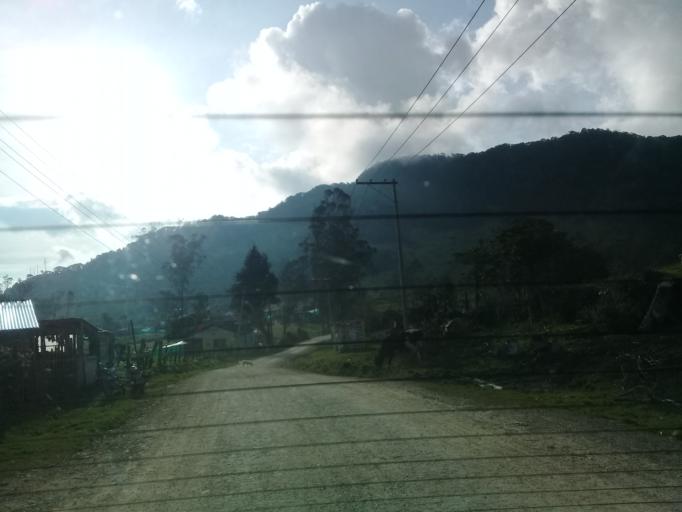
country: CO
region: Cundinamarca
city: Sibate
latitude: 4.4274
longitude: -74.2901
